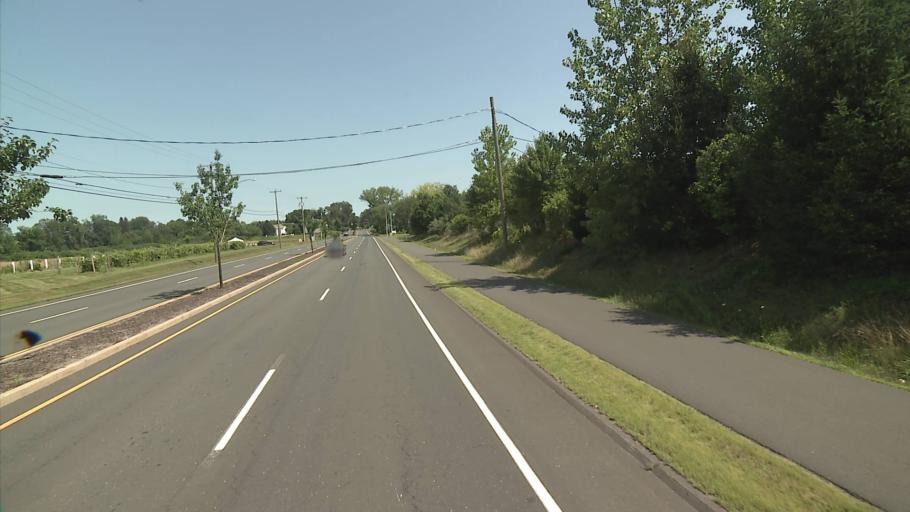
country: US
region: Connecticut
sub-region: Hartford County
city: Tariffville
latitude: 41.9441
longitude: -72.7315
